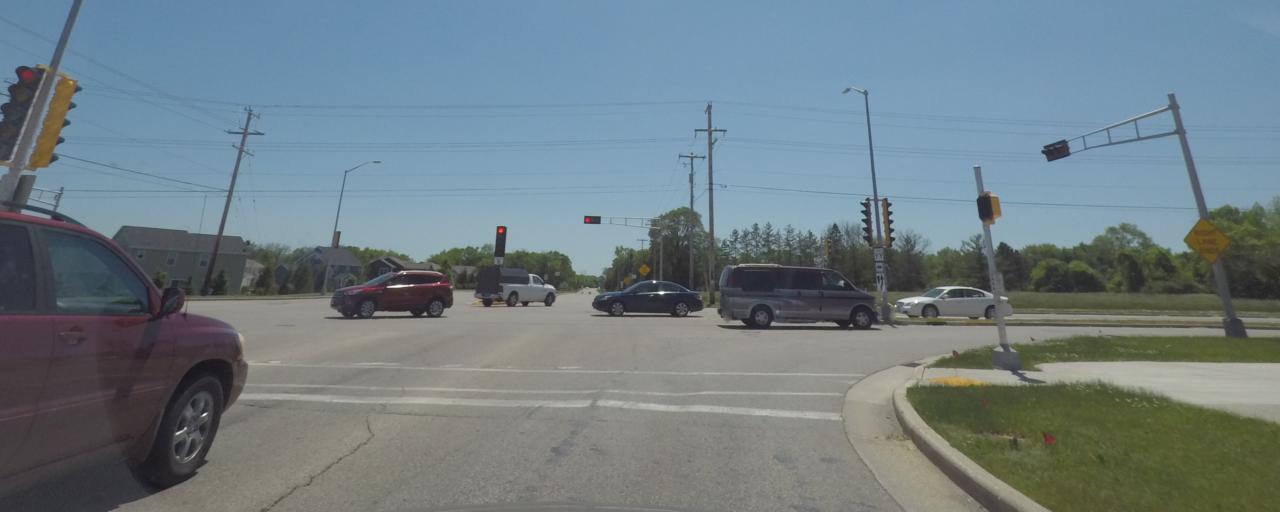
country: US
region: Wisconsin
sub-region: Waukesha County
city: Butler
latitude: 43.1050
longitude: -88.1058
